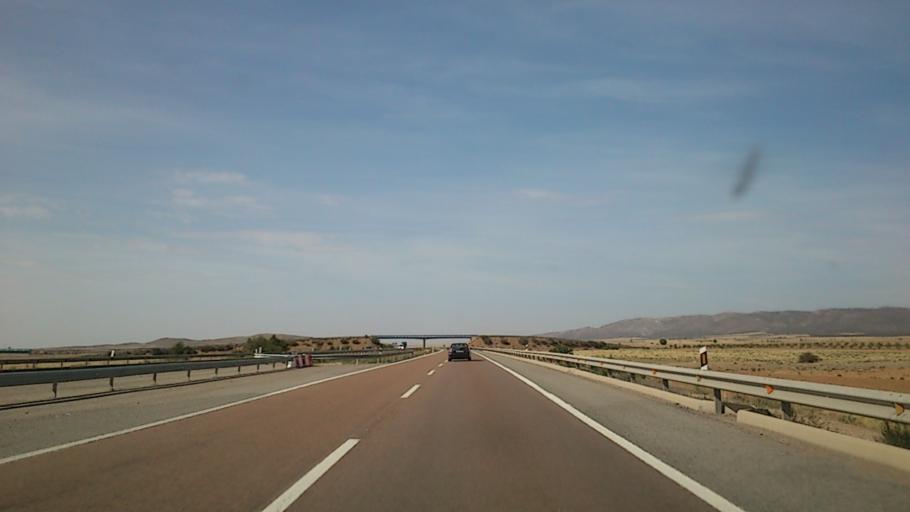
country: ES
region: Aragon
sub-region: Provincia de Teruel
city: Santa Eulalia
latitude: 40.6002
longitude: -1.2854
